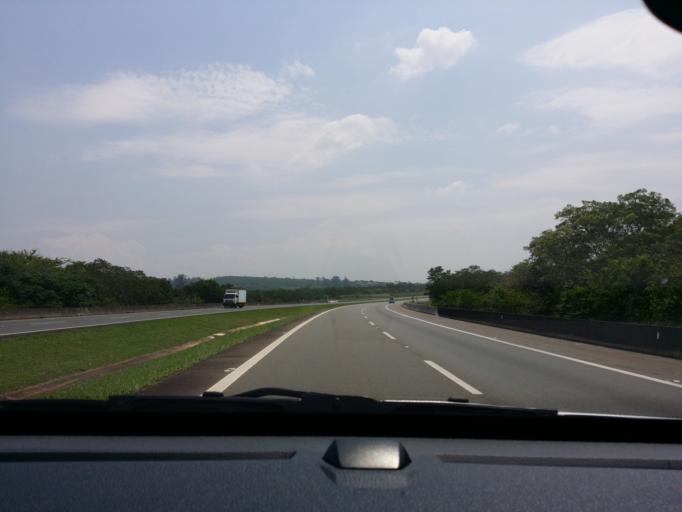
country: BR
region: Sao Paulo
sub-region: Santa Barbara D'Oeste
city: Santa Barbara d'Oeste
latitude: -22.7303
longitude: -47.4628
